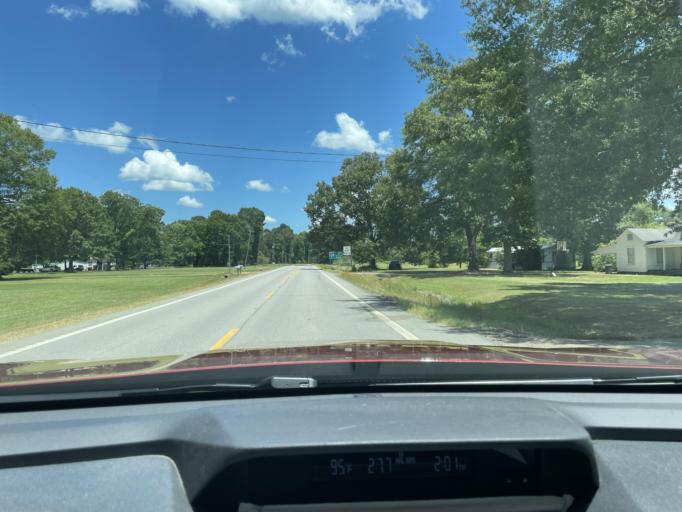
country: US
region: Arkansas
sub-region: Drew County
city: Monticello
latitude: 33.6044
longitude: -91.7284
